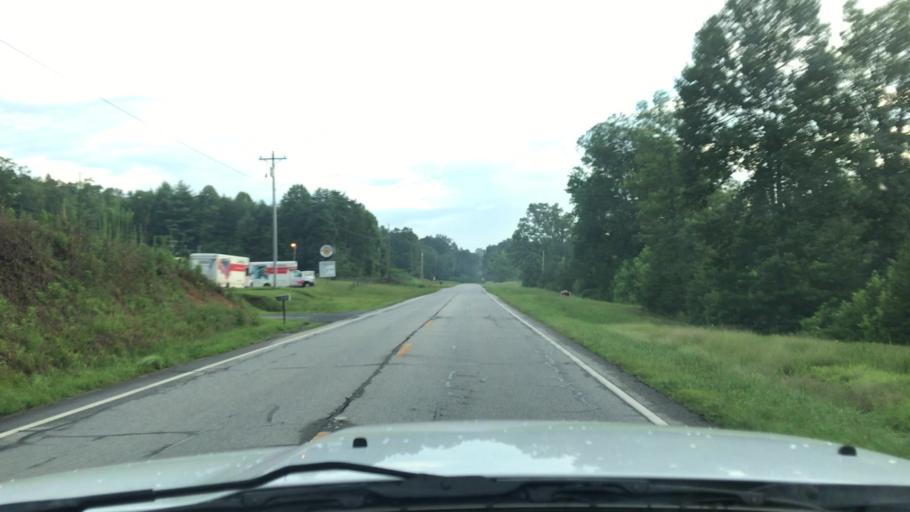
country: US
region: Georgia
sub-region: Fannin County
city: Blue Ridge
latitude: 34.9569
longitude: -84.2287
